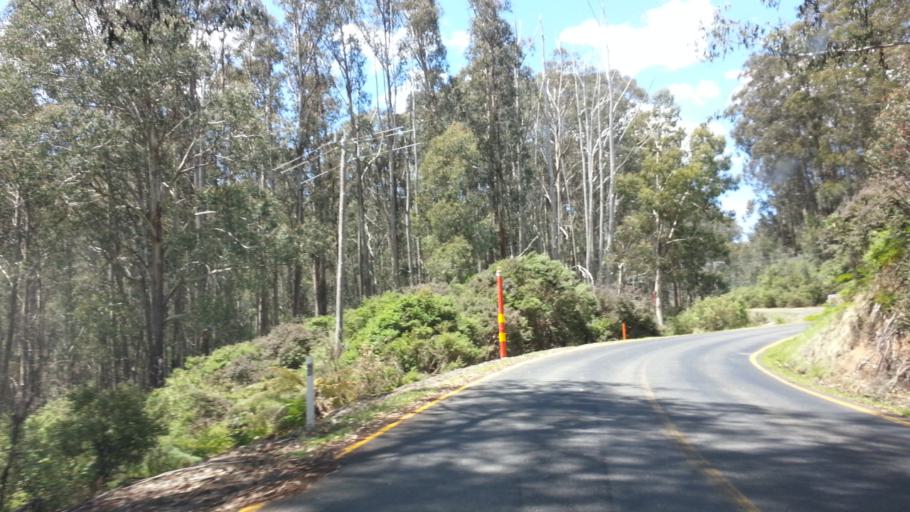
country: AU
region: Victoria
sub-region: Alpine
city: Mount Beauty
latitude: -36.8434
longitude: 147.2476
